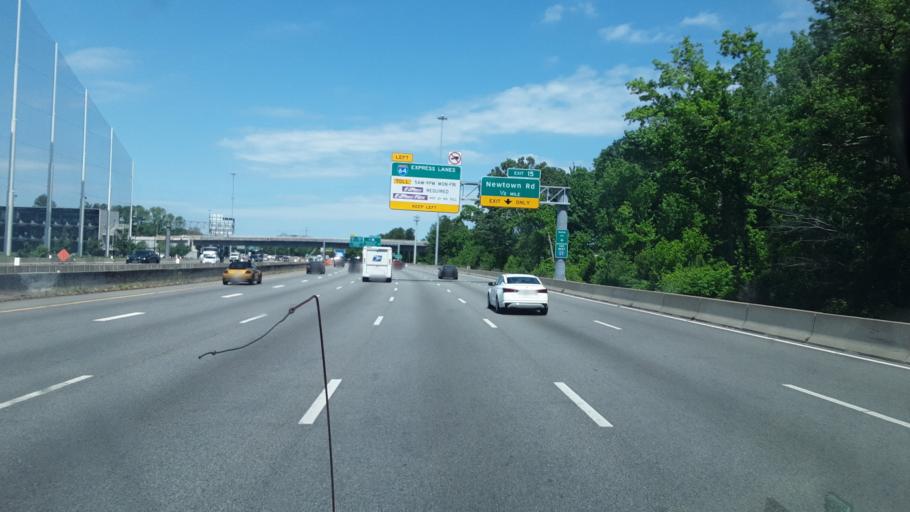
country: US
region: Virginia
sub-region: City of Chesapeake
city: Chesapeake
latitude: 36.8422
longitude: -76.1681
